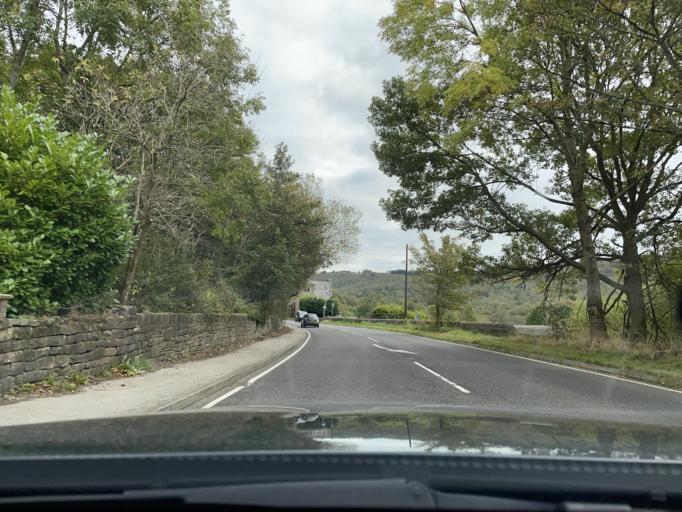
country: GB
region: England
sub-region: Sheffield
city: Bradfield
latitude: 53.3790
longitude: -1.5877
